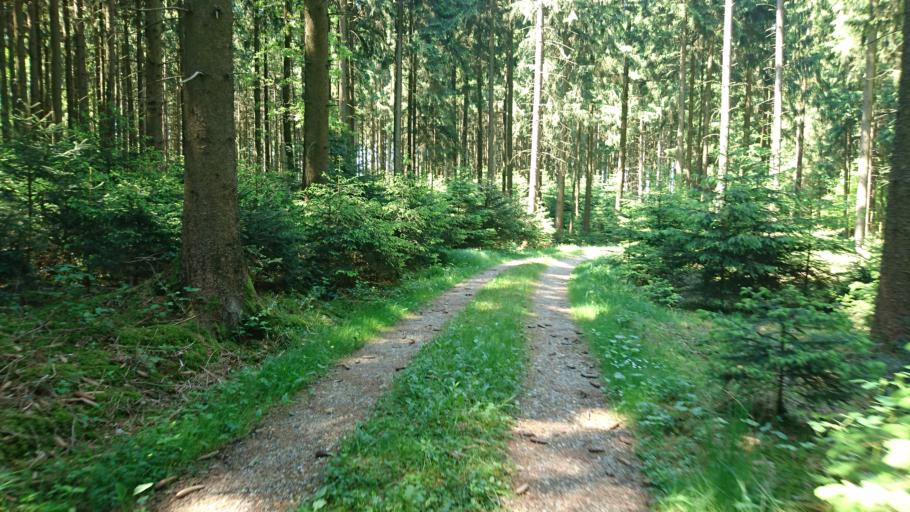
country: DE
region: Bavaria
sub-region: Lower Bavaria
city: Stallwang
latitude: 48.5281
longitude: 12.2267
